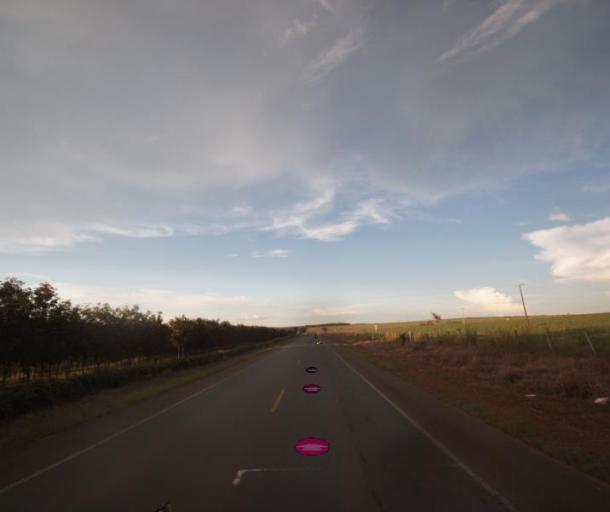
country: BR
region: Goias
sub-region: Anapolis
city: Anapolis
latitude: -16.1901
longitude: -48.9056
